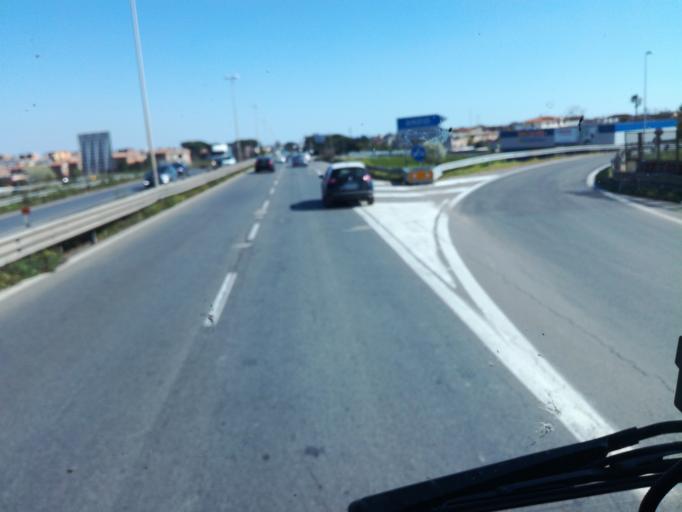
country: IT
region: Latium
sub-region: Provincia di Latina
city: Aprilia
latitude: 41.5901
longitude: 12.6385
